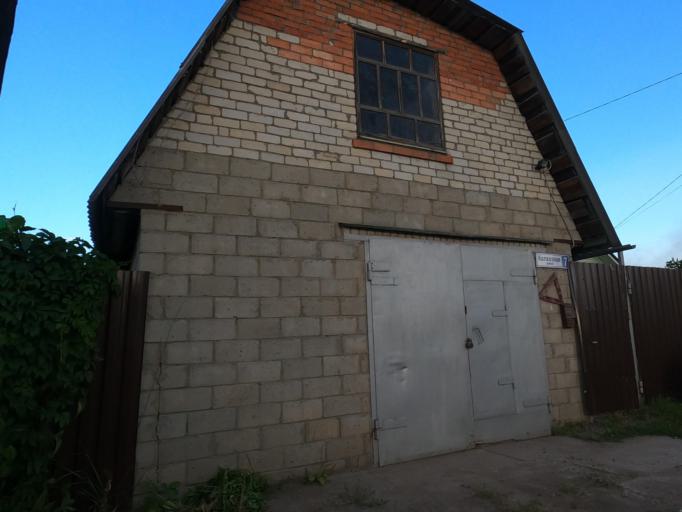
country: RU
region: Moskovskaya
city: Ashitkovo
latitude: 55.4189
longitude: 38.5802
